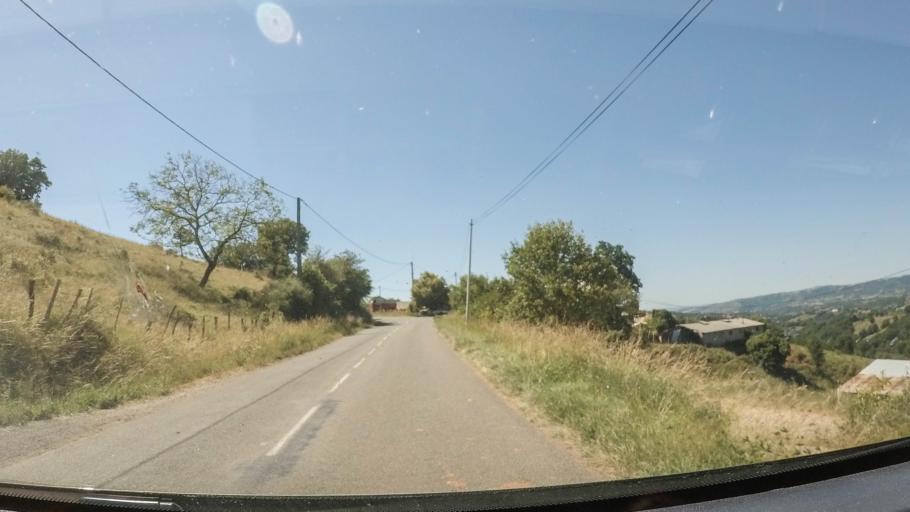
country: FR
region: Midi-Pyrenees
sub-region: Departement de l'Aveyron
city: Saint-Christophe-Vallon
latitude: 44.4711
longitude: 2.3647
